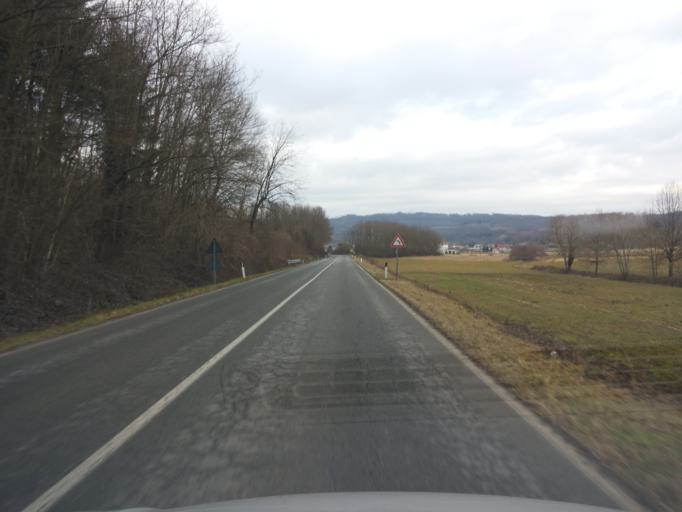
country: IT
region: Piedmont
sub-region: Provincia di Torino
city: Borgomasino
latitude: 45.3477
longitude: 7.9909
